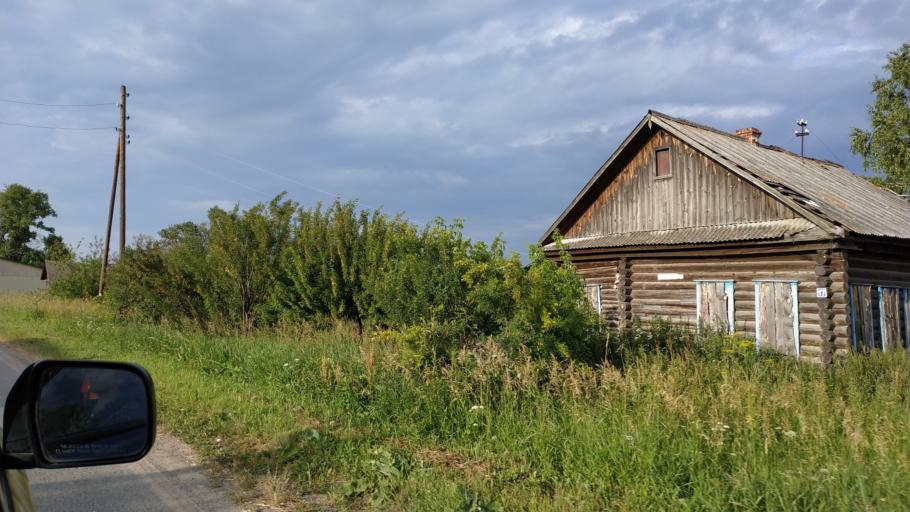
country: RU
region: Sverdlovsk
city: Yelanskiy
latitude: 57.0827
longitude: 62.4751
